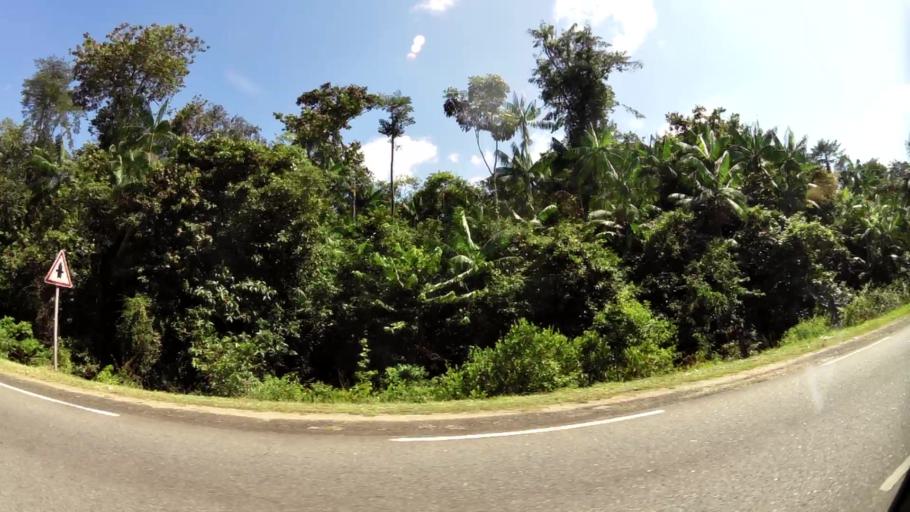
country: GF
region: Guyane
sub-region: Guyane
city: Matoury
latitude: 4.8370
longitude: -52.3425
